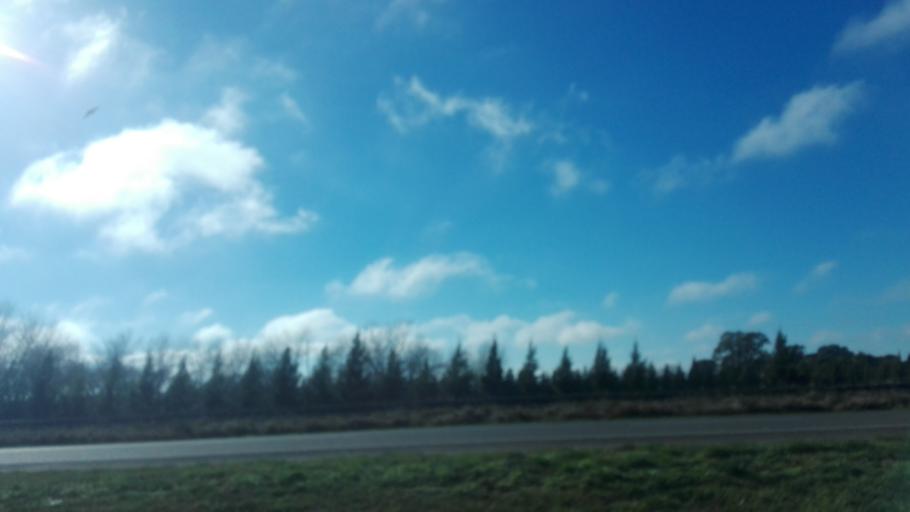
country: AR
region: Buenos Aires
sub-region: Partido de Castelli
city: Castelli
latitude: -35.8406
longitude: -57.9103
